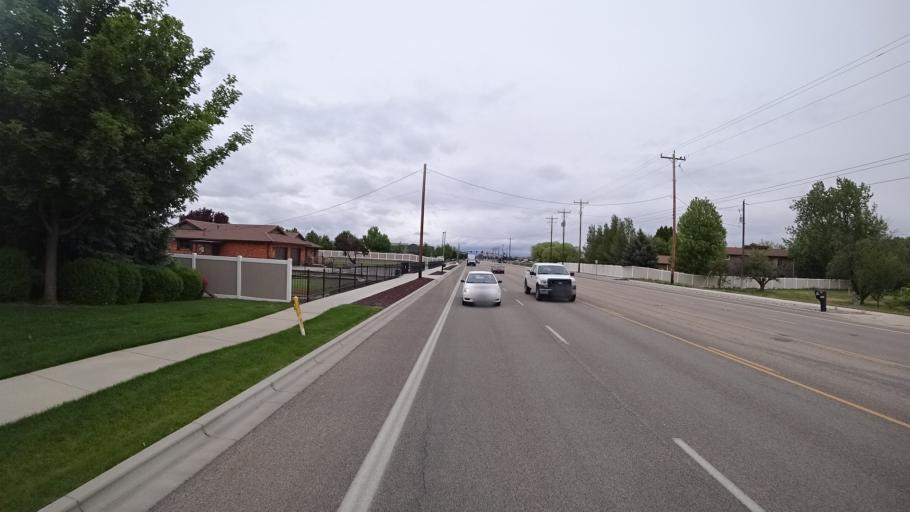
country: US
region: Idaho
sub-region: Ada County
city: Meridian
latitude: 43.6339
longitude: -116.3615
